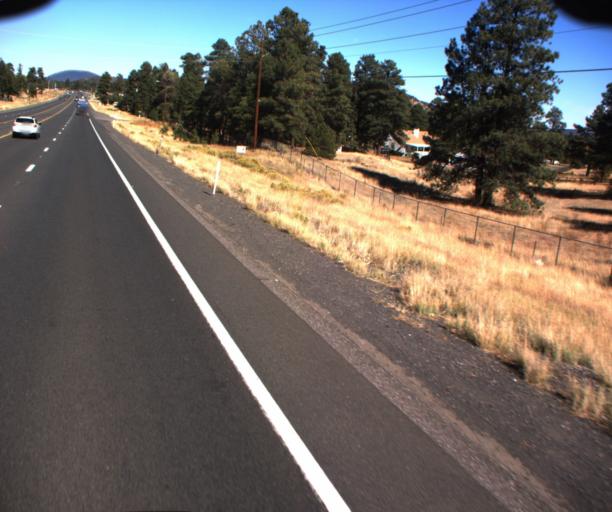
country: US
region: Arizona
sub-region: Coconino County
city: Flagstaff
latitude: 35.2642
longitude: -111.5479
